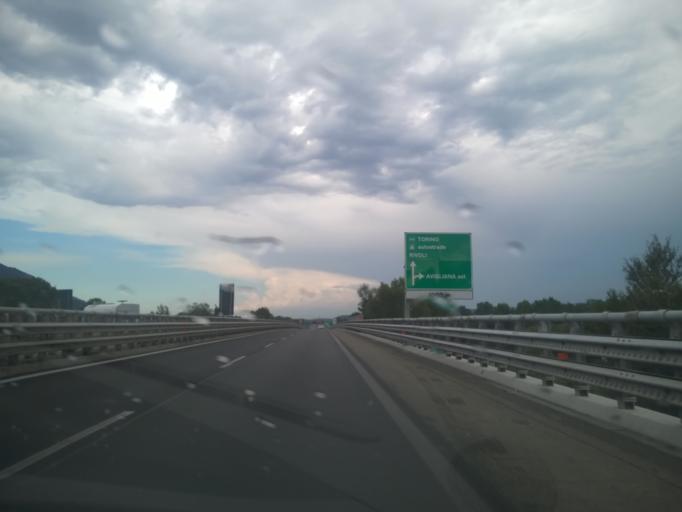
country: IT
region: Piedmont
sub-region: Provincia di Torino
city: Avigliana
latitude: 45.0930
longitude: 7.4042
